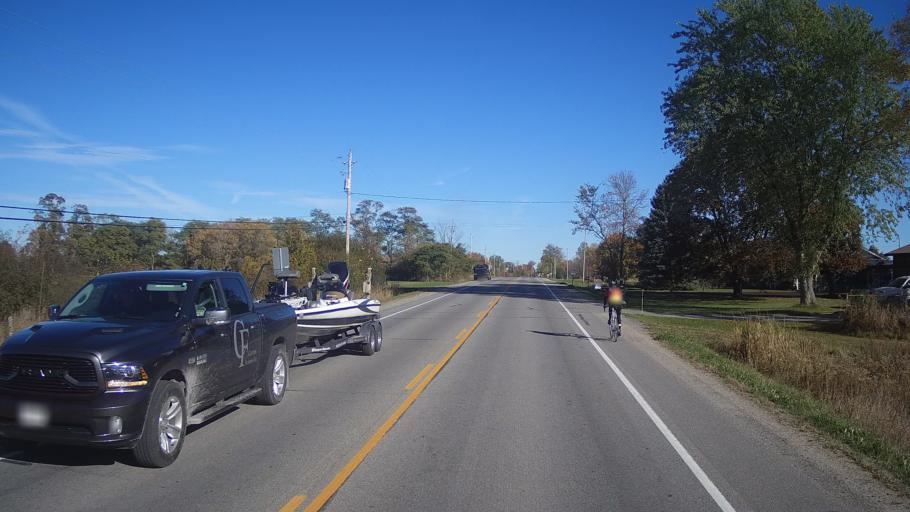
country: CA
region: Ontario
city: Kingston
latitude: 44.4073
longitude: -76.5659
